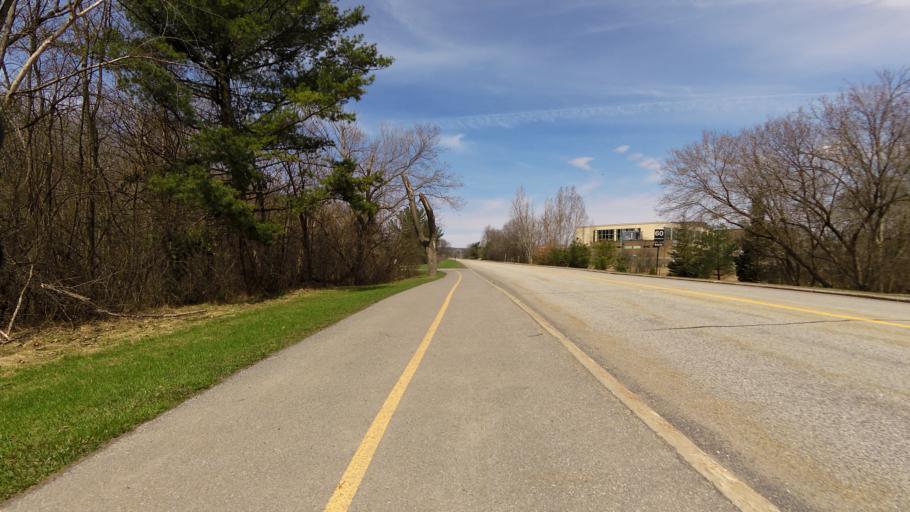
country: CA
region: Ontario
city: Ottawa
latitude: 45.4261
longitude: -75.7374
